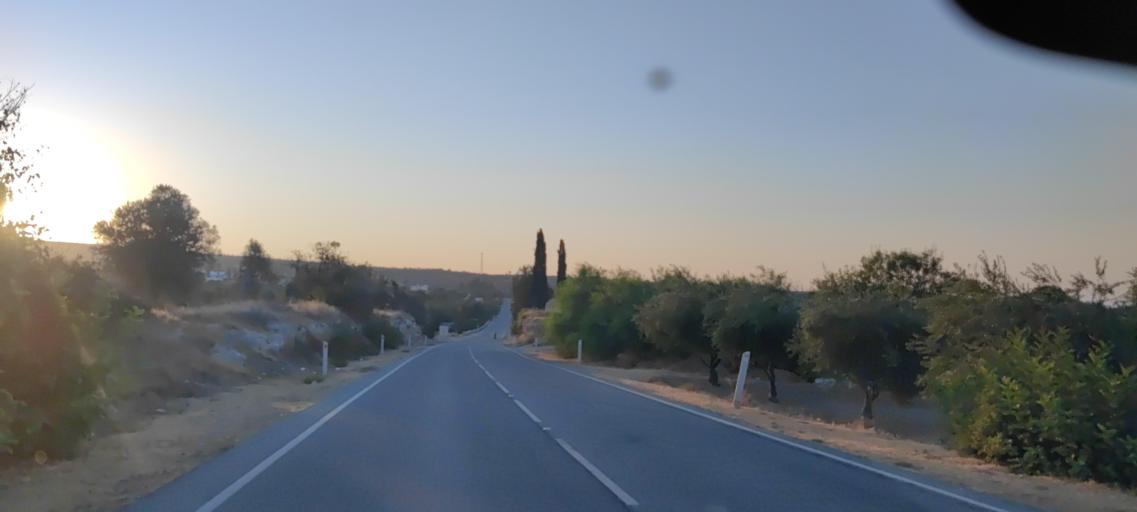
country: CY
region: Limassol
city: Pissouri
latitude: 34.6778
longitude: 32.7843
